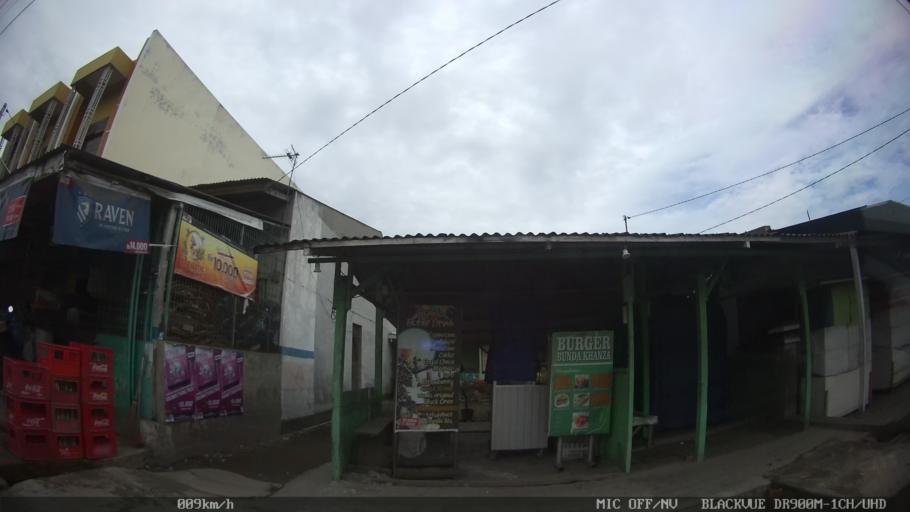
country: ID
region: North Sumatra
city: Sunggal
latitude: 3.6423
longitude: 98.5940
